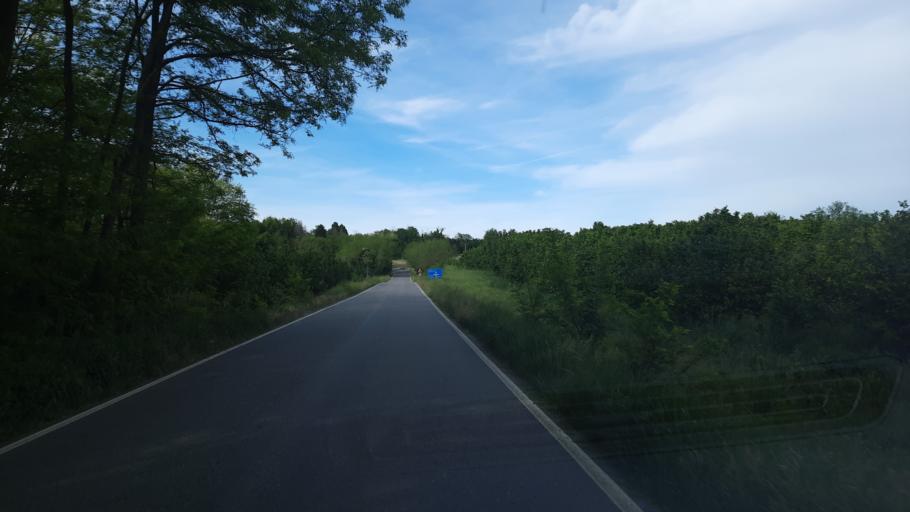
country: IT
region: Piedmont
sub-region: Provincia di Alessandria
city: Castelletto Merli
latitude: 45.0603
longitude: 8.2375
